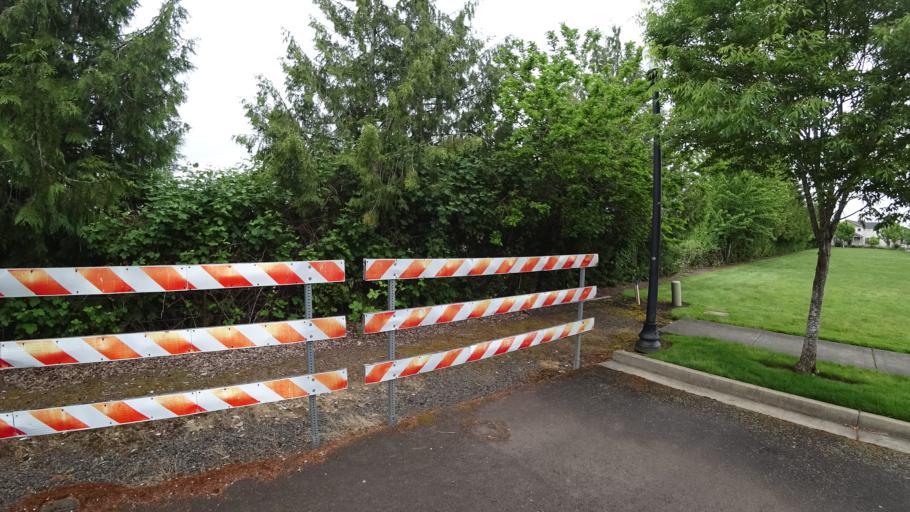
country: US
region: Oregon
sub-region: Washington County
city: Aloha
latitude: 45.4947
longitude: -122.9233
